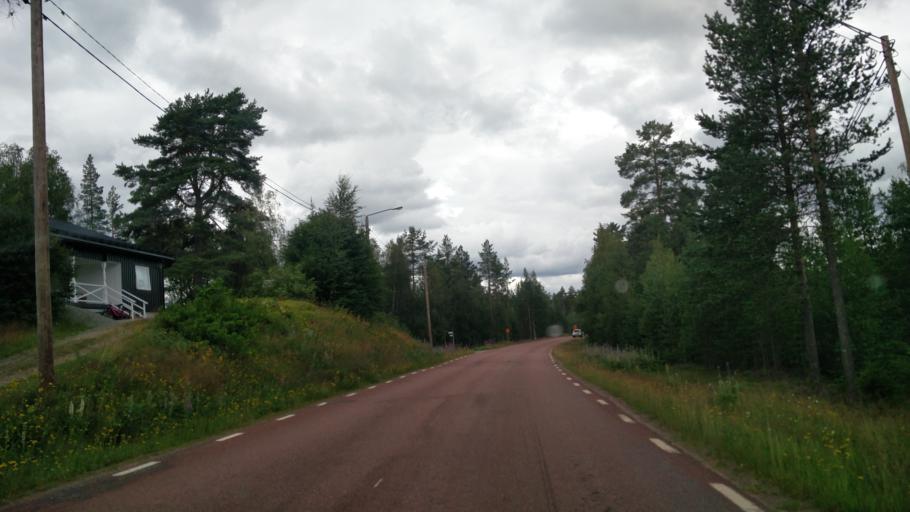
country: NO
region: Hedmark
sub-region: Trysil
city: Innbygda
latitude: 61.1373
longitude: 12.8076
